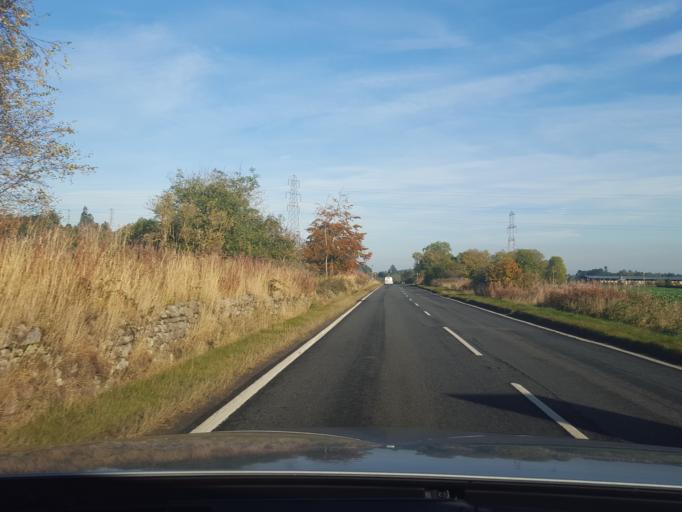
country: GB
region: Scotland
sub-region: Highland
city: Inverness
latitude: 57.4460
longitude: -4.2915
